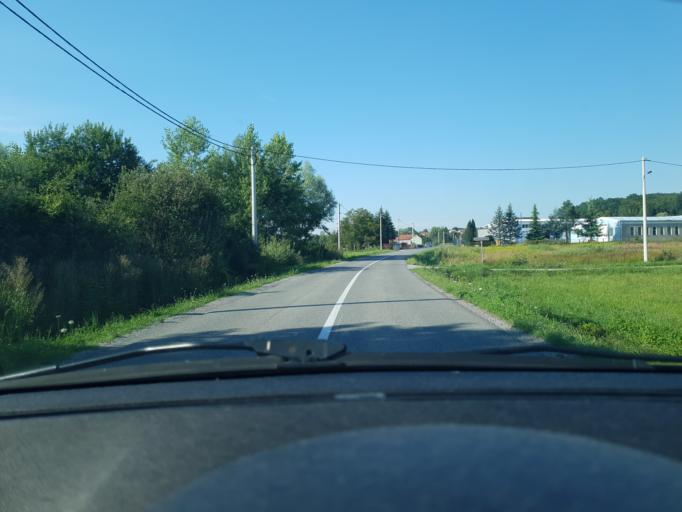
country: HR
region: Zagrebacka
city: Jakovlje
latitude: 45.9272
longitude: 15.8427
